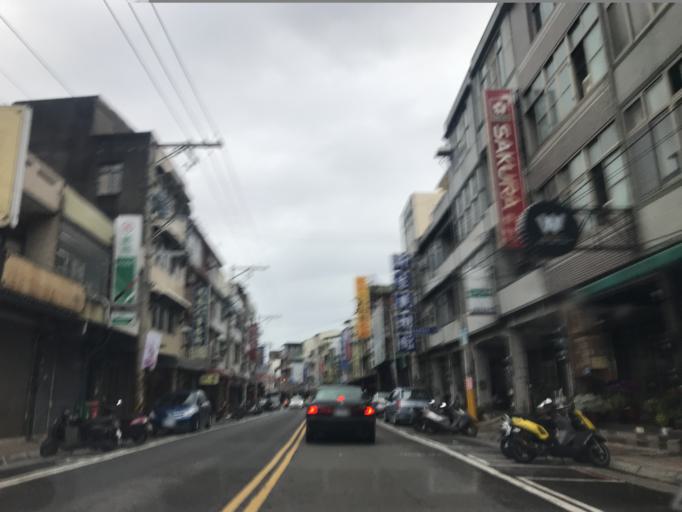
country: TW
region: Taiwan
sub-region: Hsinchu
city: Zhubei
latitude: 24.8280
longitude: 121.0763
